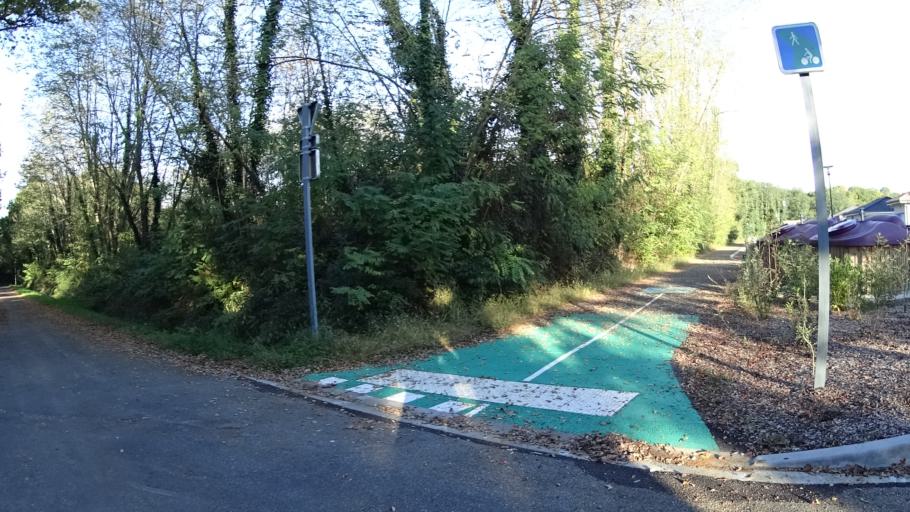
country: FR
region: Aquitaine
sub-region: Departement des Landes
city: Saint-Paul-les-Dax
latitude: 43.7423
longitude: -1.0488
